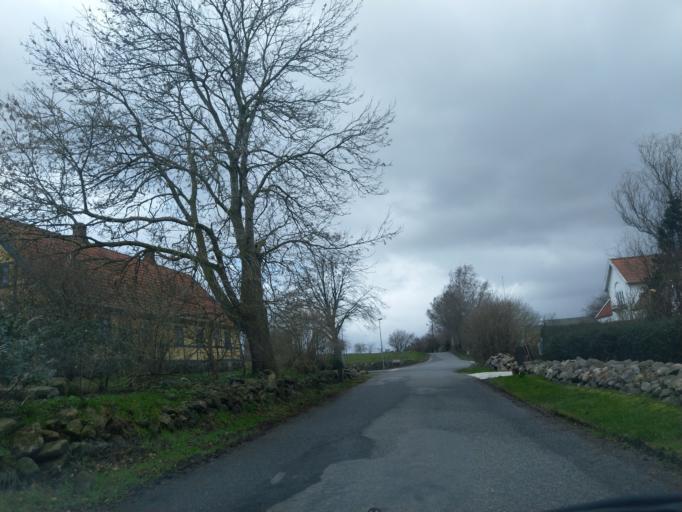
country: DK
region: Zealand
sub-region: Naestved Kommune
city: Fuglebjerg
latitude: 55.3525
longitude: 11.5784
